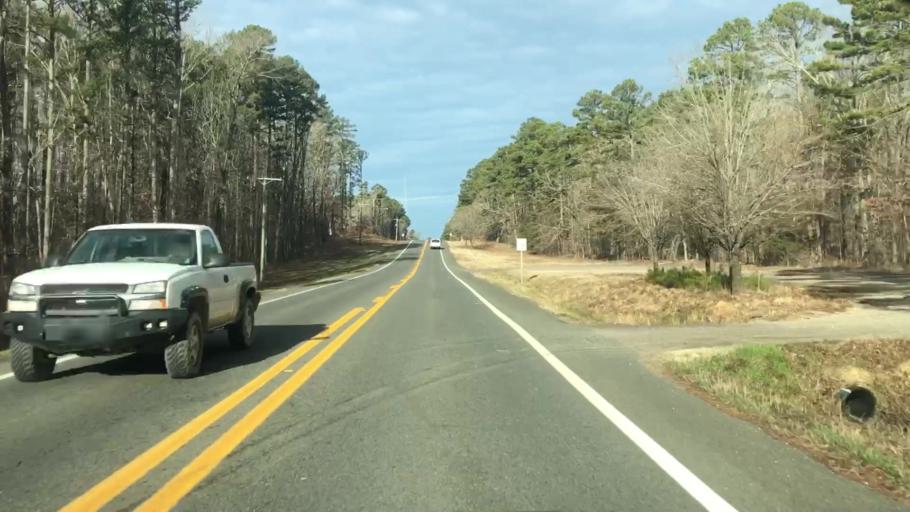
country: US
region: Arkansas
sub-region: Montgomery County
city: Mount Ida
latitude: 34.5415
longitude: -93.6089
